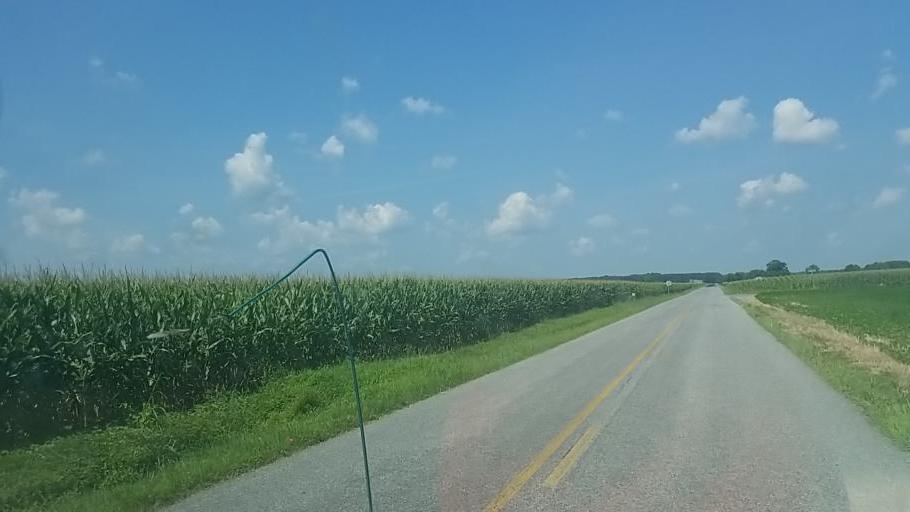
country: US
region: Maryland
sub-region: Worcester County
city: Berlin
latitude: 38.2943
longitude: -75.2525
